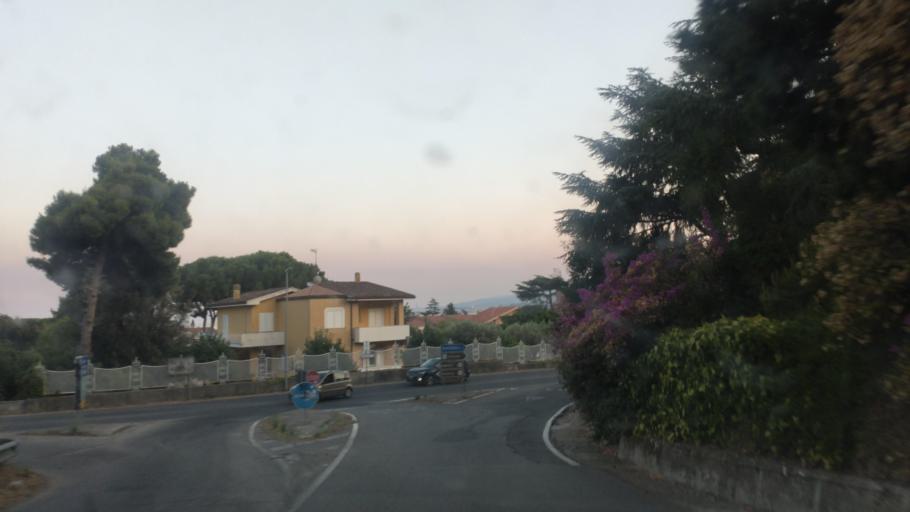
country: IT
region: Calabria
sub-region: Provincia di Catanzaro
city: Montepaone Lido
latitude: 38.7433
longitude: 16.5524
